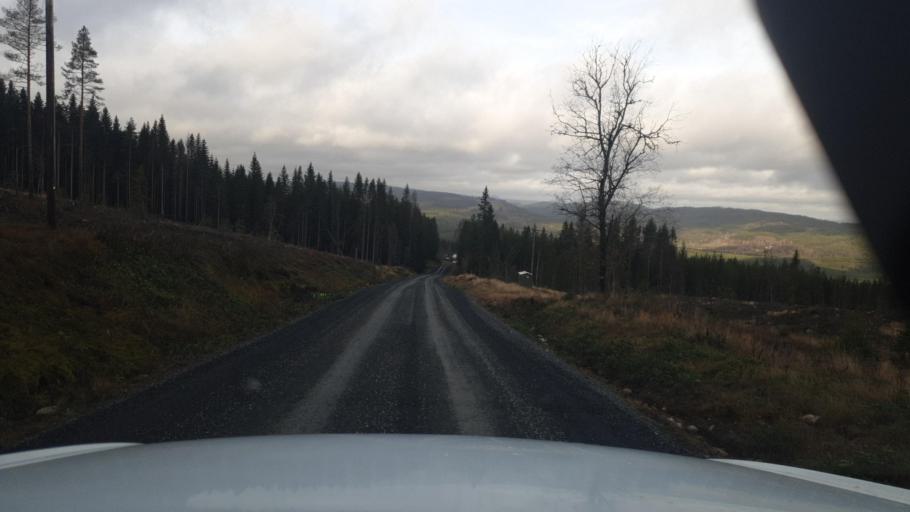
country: SE
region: Vaermland
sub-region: Torsby Kommun
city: Torsby
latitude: 60.1771
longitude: 12.6456
